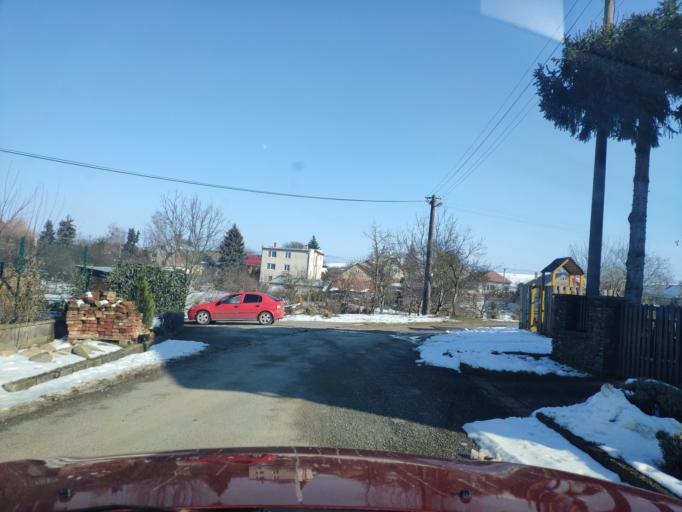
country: HU
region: Borsod-Abauj-Zemplen
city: Gonc
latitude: 48.5800
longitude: 21.2723
